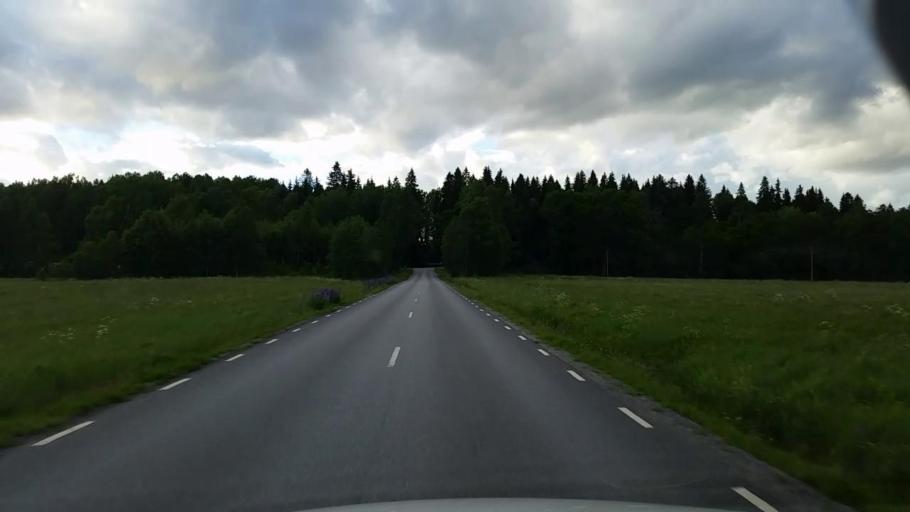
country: SE
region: Vaestmanland
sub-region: Skinnskattebergs Kommun
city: Skinnskatteberg
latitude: 59.7736
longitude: 15.8529
